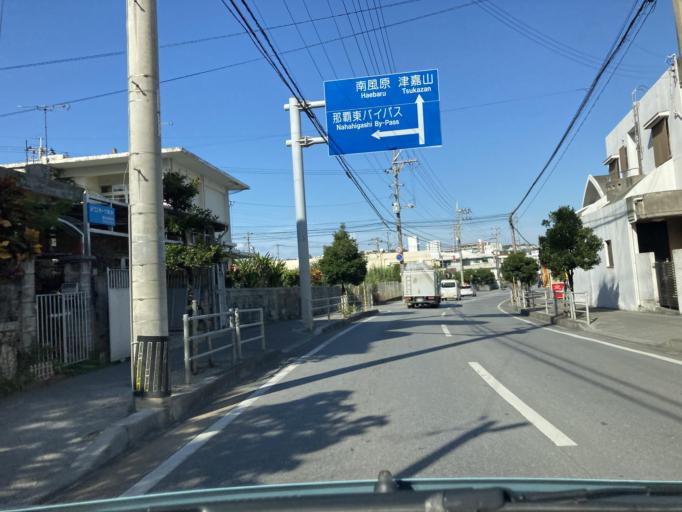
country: JP
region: Okinawa
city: Tomigusuku
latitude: 26.1847
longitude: 127.7073
